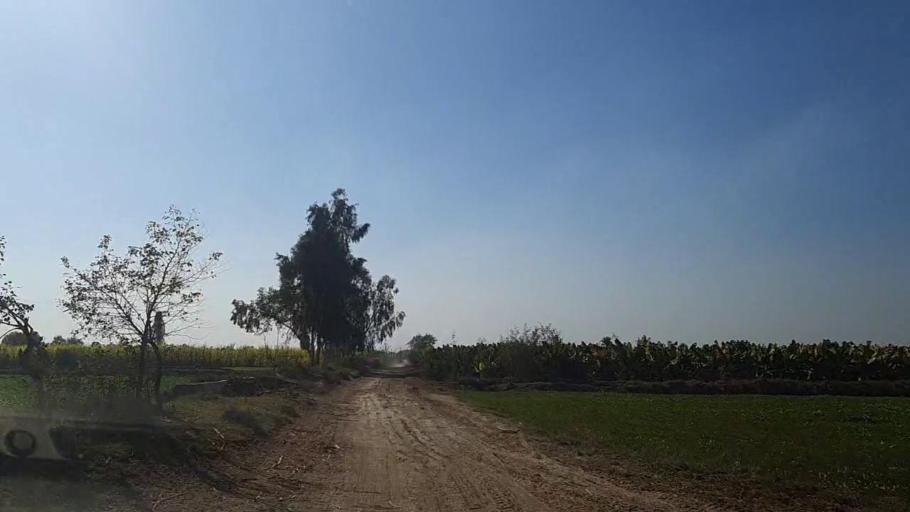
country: PK
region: Sindh
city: Sakrand
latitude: 26.2338
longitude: 68.1774
